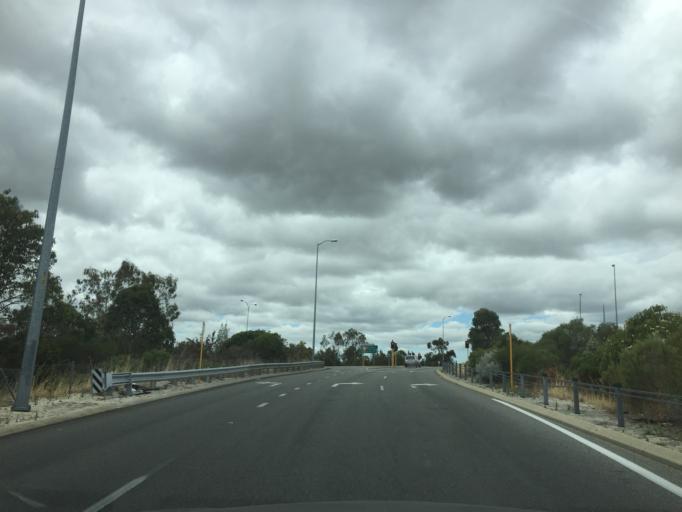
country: AU
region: Western Australia
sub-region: Canning
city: Canning Vale
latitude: -32.0533
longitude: 115.9303
